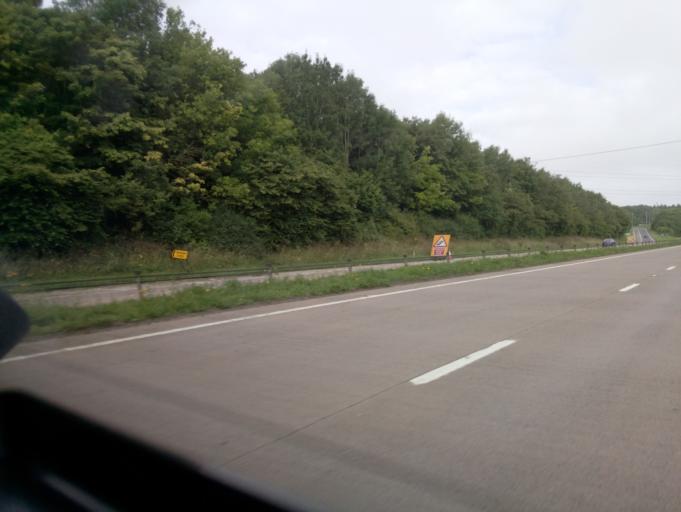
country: GB
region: England
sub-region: Gloucestershire
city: Cirencester
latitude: 51.7207
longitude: -1.9436
